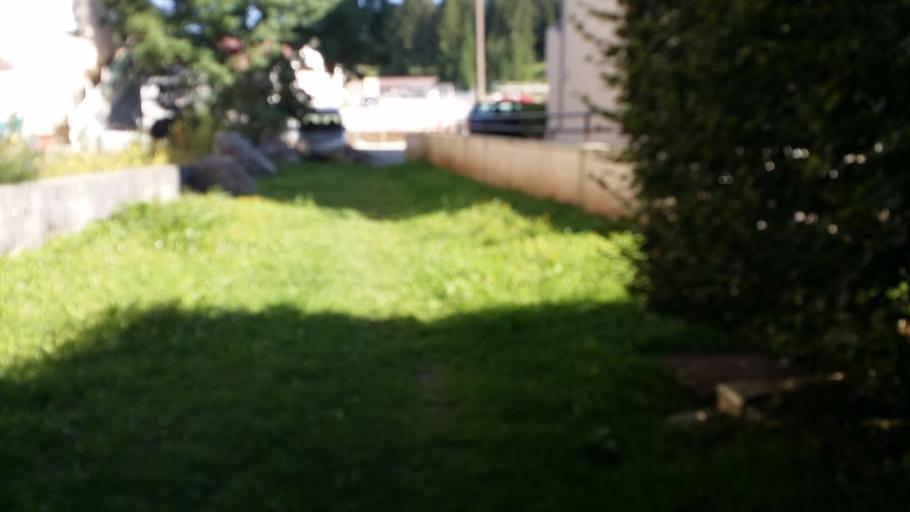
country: FR
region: Franche-Comte
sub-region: Departement du Jura
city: Les Rousses
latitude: 46.4849
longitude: 6.0585
